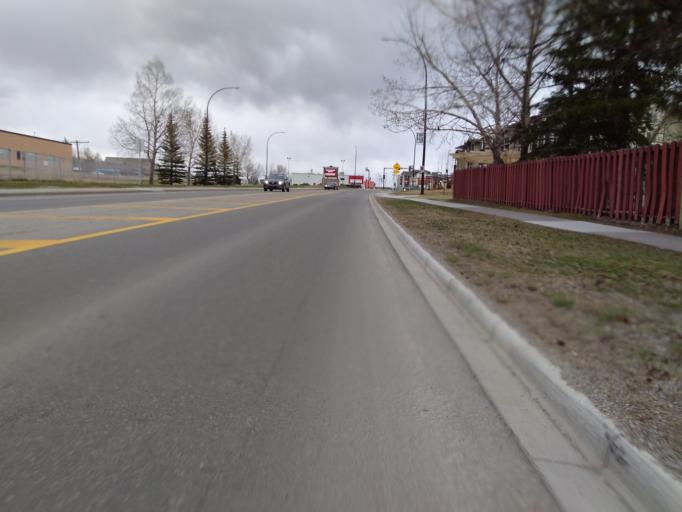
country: CA
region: Alberta
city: Cochrane
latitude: 51.1918
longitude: -114.4759
